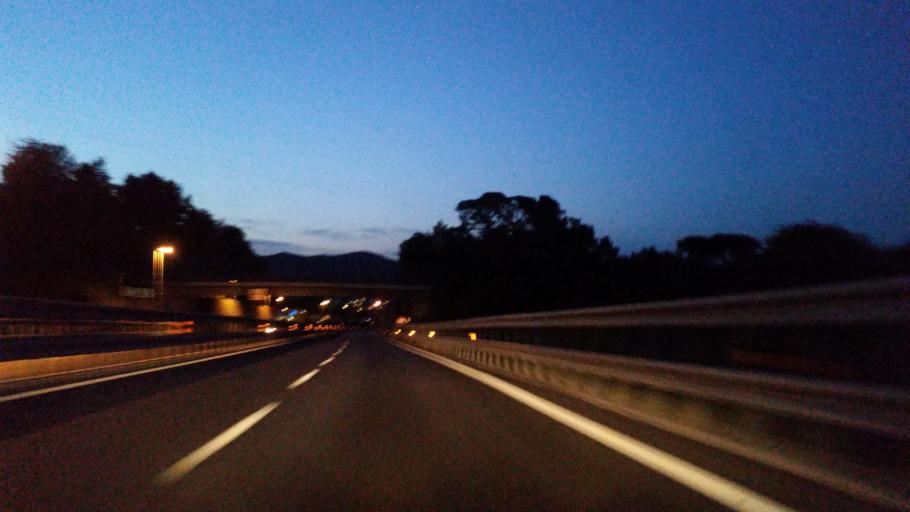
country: IT
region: Liguria
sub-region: Provincia di Savona
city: Andora
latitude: 43.9557
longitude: 8.1349
